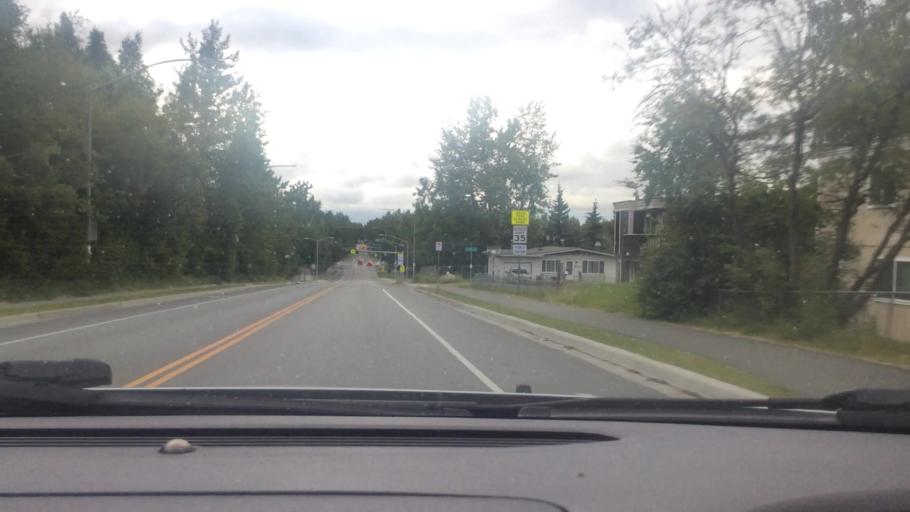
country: US
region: Alaska
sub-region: Anchorage Municipality
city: Anchorage
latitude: 61.1917
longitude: -149.7634
